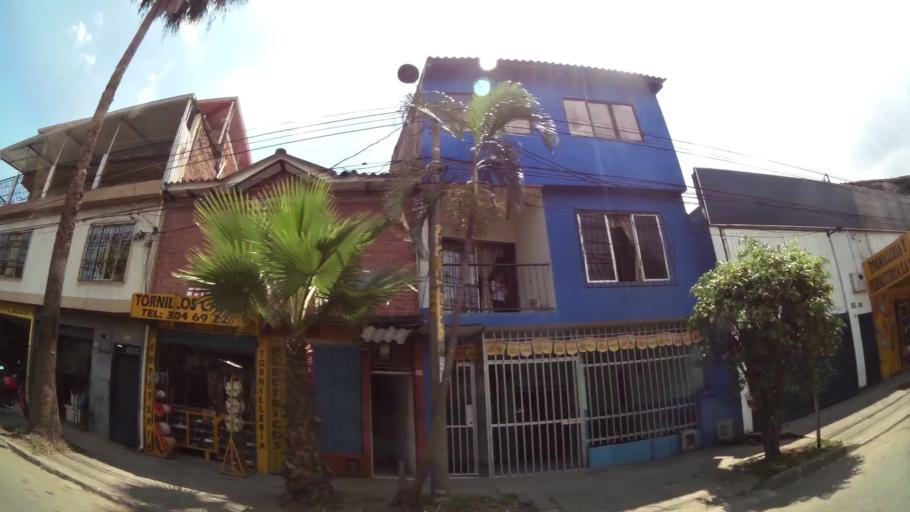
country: CO
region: Valle del Cauca
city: Cali
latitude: 3.4537
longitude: -76.5091
